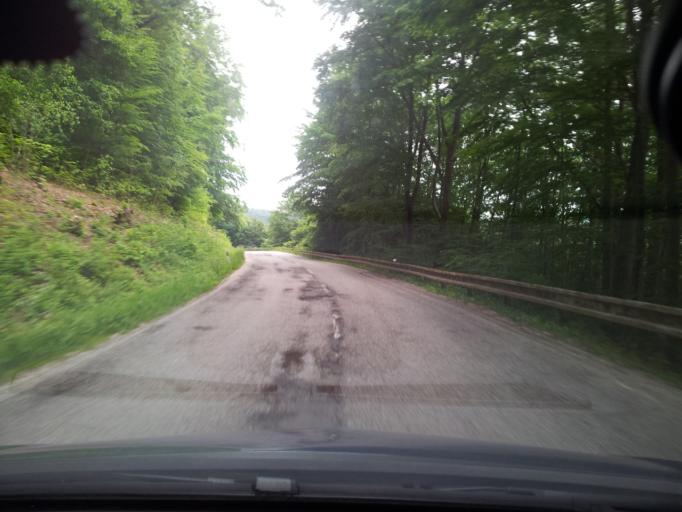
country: SK
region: Nitriansky
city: Partizanske
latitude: 48.5764
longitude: 18.4551
